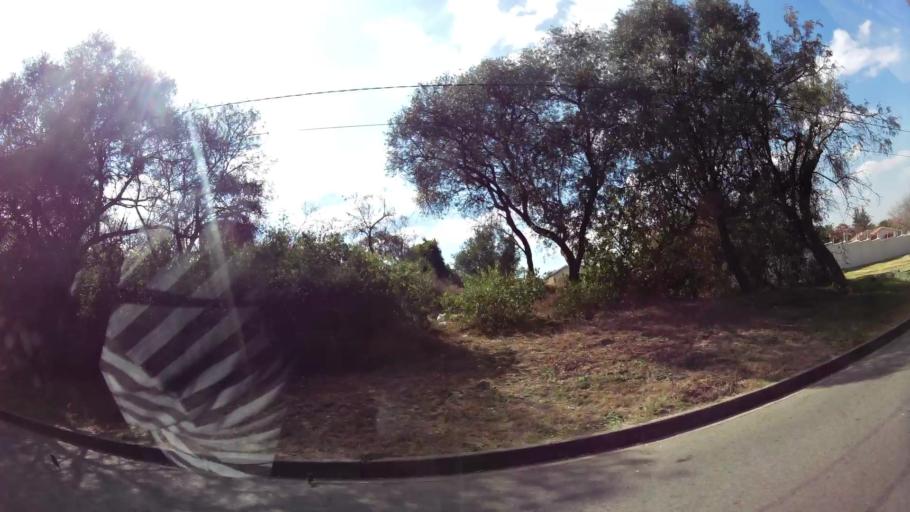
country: ZA
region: Gauteng
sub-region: West Rand District Municipality
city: Muldersdriseloop
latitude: -26.0675
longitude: 27.9592
